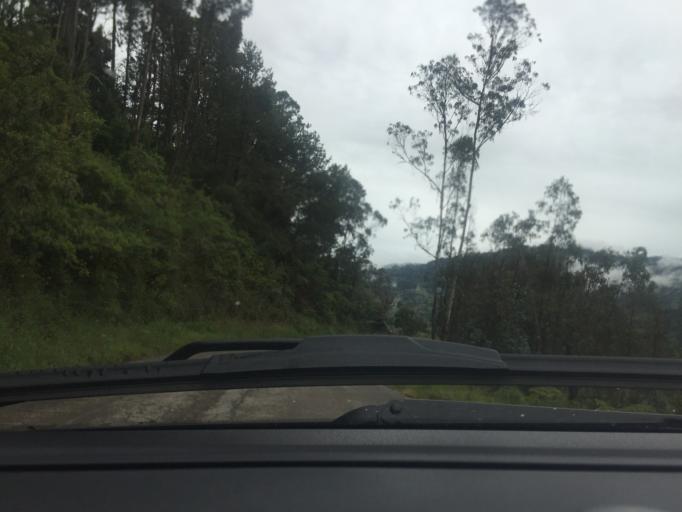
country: CO
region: Cundinamarca
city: Junin
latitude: 4.8106
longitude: -73.7126
